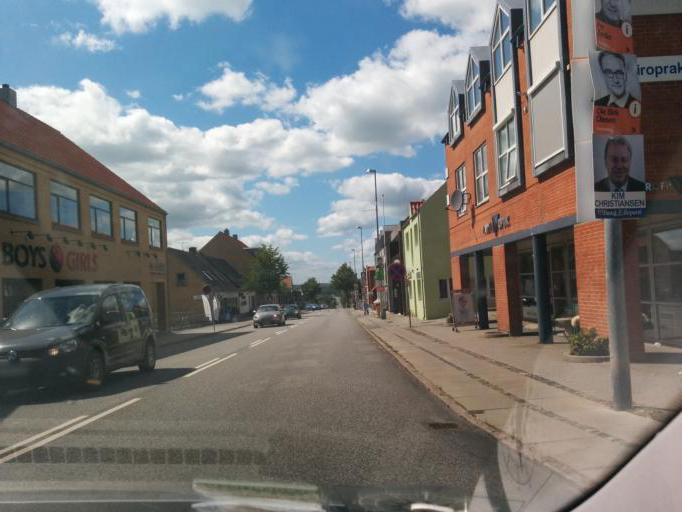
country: DK
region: Central Jutland
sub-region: Syddjurs Kommune
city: Ronde
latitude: 56.3005
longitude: 10.4773
